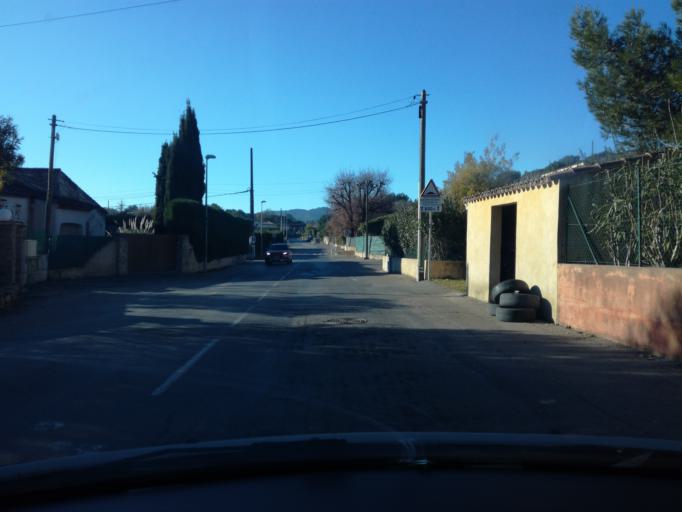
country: FR
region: Provence-Alpes-Cote d'Azur
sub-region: Departement des Alpes-Maritimes
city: La Roquette-sur-Siagne
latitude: 43.6052
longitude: 6.9551
